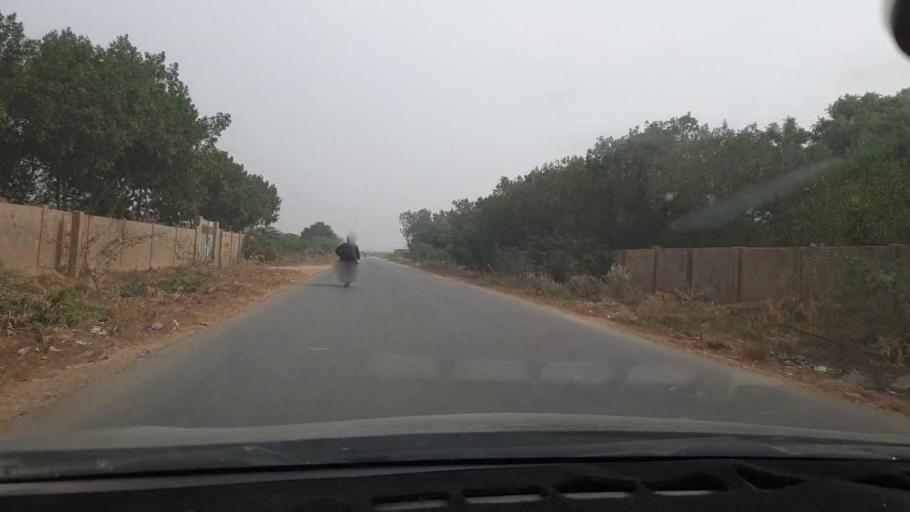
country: PK
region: Sindh
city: Malir Cantonment
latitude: 24.9141
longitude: 67.2702
